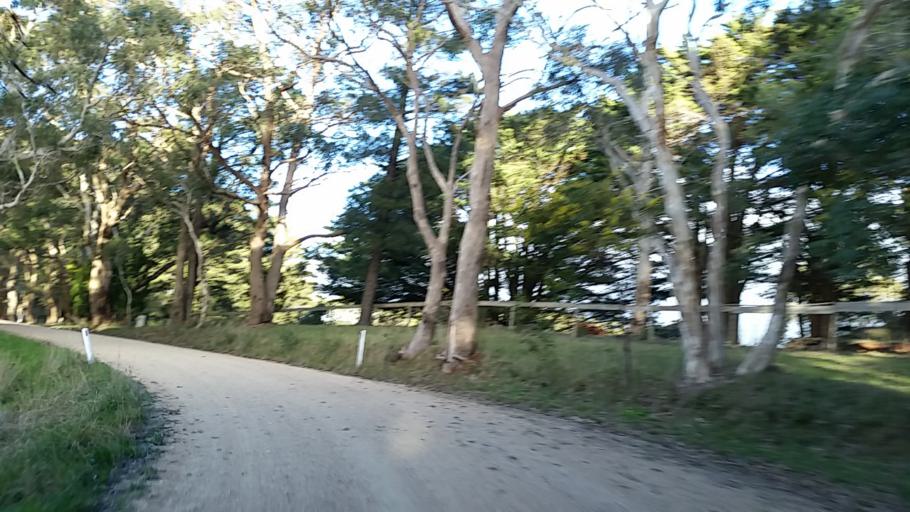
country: AU
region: South Australia
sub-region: Adelaide Hills
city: Lobethal
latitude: -34.9034
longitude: 138.8047
